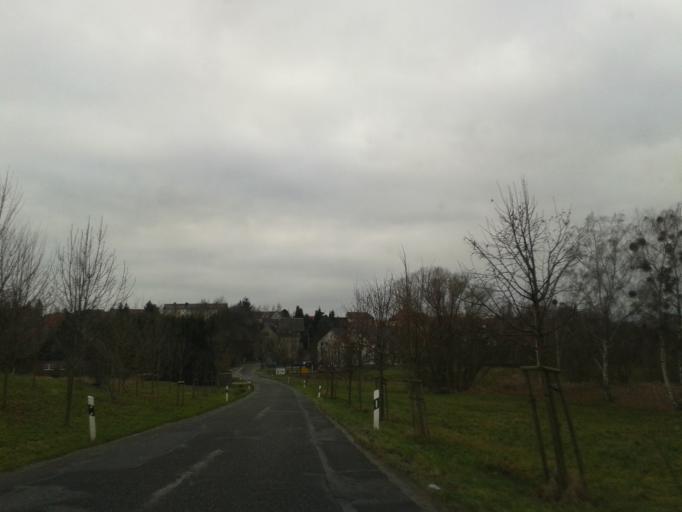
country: DE
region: Saxony
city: Weissenberg
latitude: 51.2007
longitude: 14.6628
